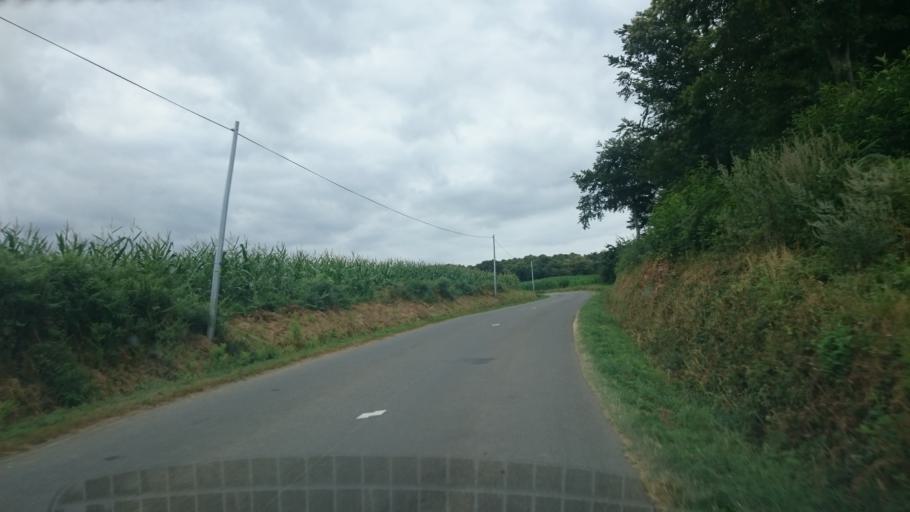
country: FR
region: Brittany
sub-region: Departement d'Ille-et-Vilaine
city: Saint-Domineuc
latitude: 48.4087
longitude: -1.8561
